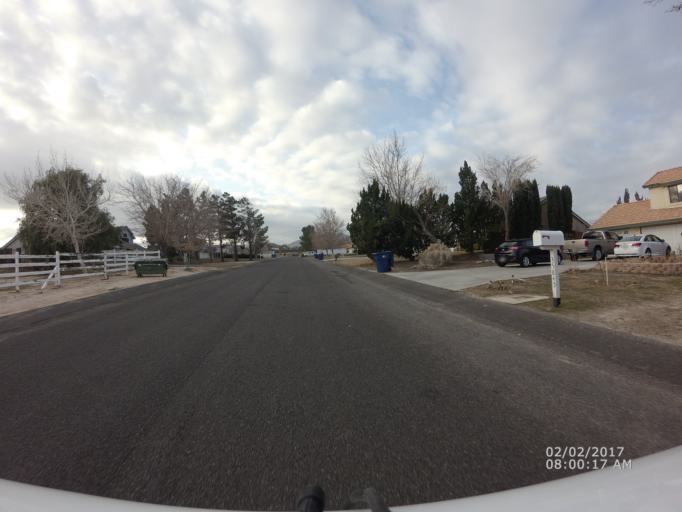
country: US
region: California
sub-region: Los Angeles County
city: Littlerock
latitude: 34.5331
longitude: -118.0437
